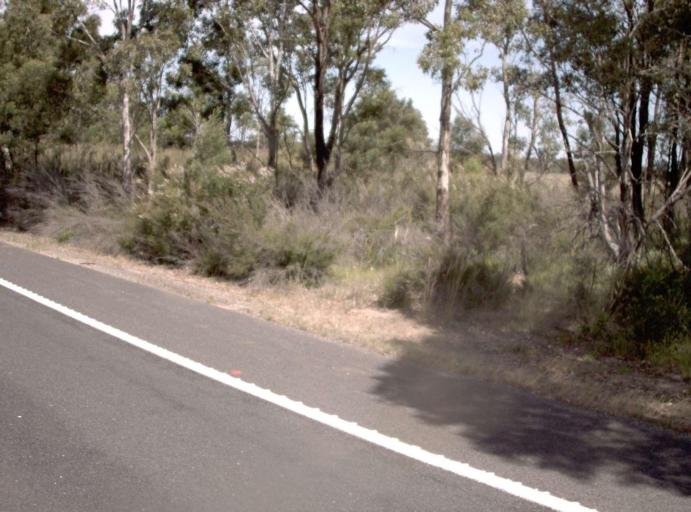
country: AU
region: Victoria
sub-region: Wellington
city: Sale
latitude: -37.9197
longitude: 147.2651
